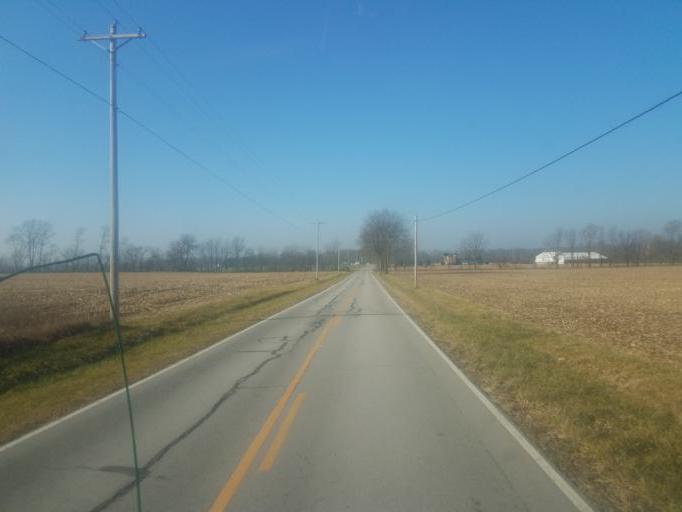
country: US
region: Ohio
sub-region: Seneca County
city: Tiffin
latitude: 41.0521
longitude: -83.0420
